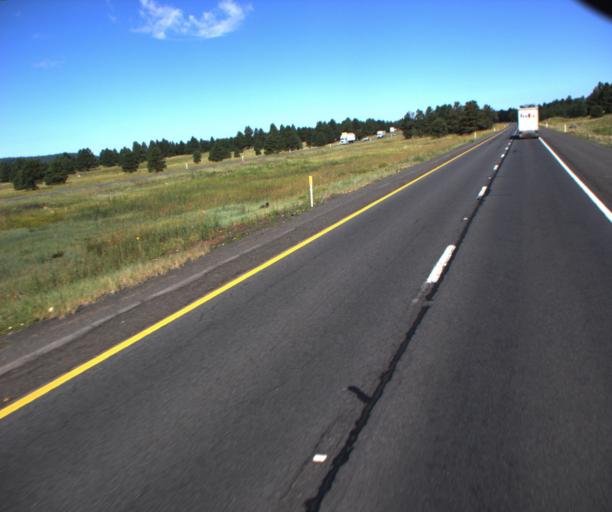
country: US
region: Arizona
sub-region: Coconino County
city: Parks
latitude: 35.2432
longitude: -111.8366
